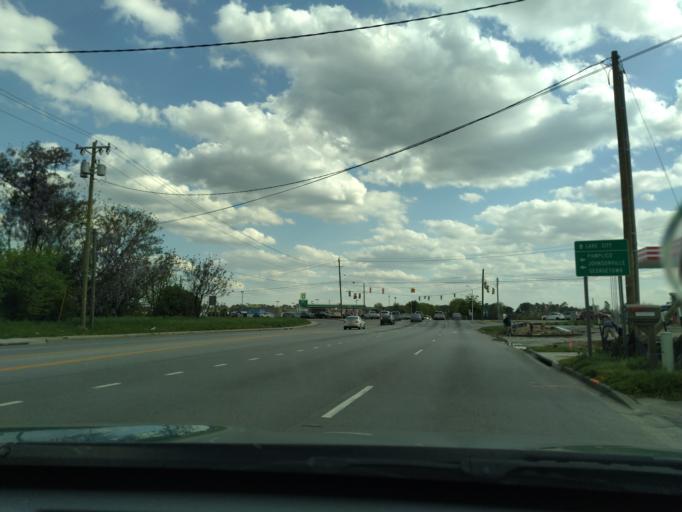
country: US
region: South Carolina
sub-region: Florence County
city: Florence
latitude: 34.1652
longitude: -79.7602
